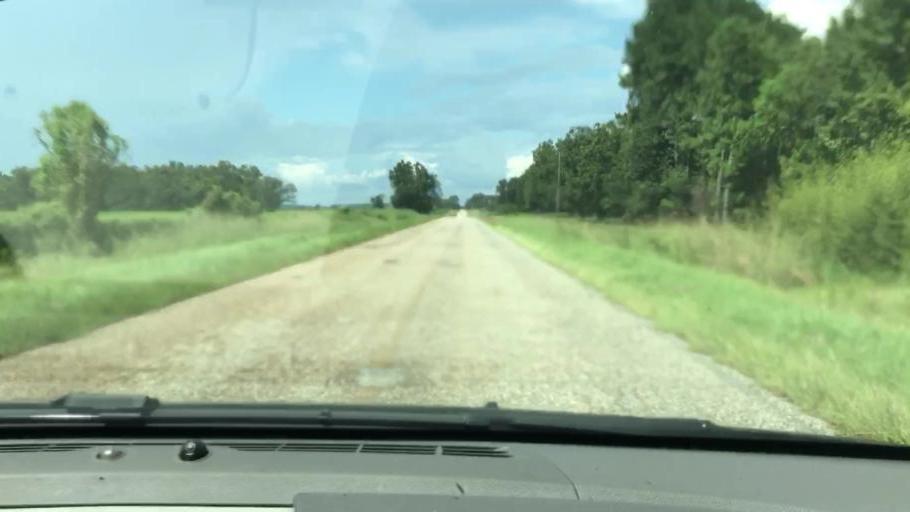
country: US
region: Georgia
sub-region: Seminole County
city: Donalsonville
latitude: 31.1926
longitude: -85.0040
